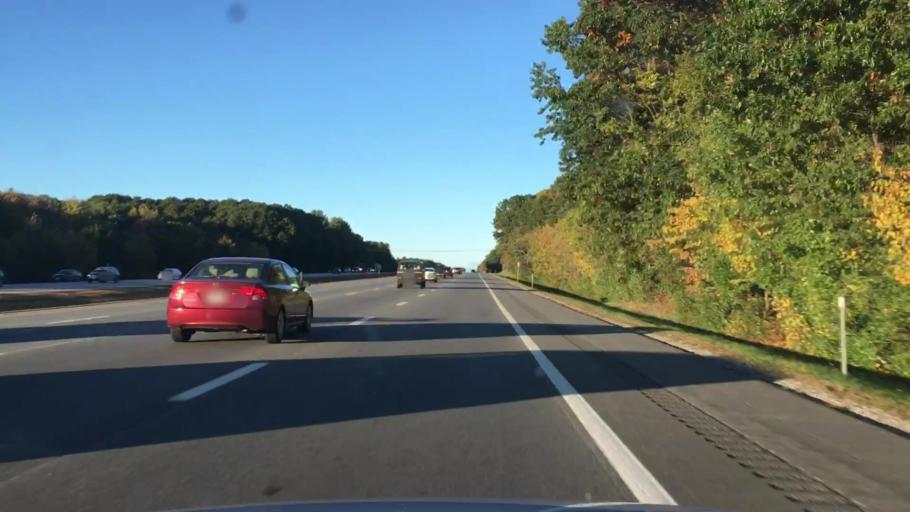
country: US
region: New Hampshire
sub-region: Rockingham County
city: North Hampton
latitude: 43.0005
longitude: -70.8438
